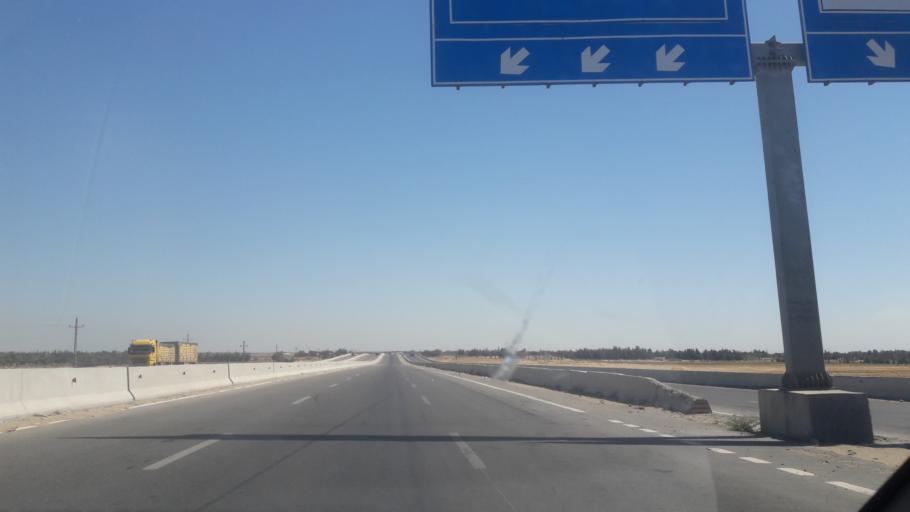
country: EG
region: Al Isma'iliyah
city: Ismailia
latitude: 30.8379
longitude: 32.1665
